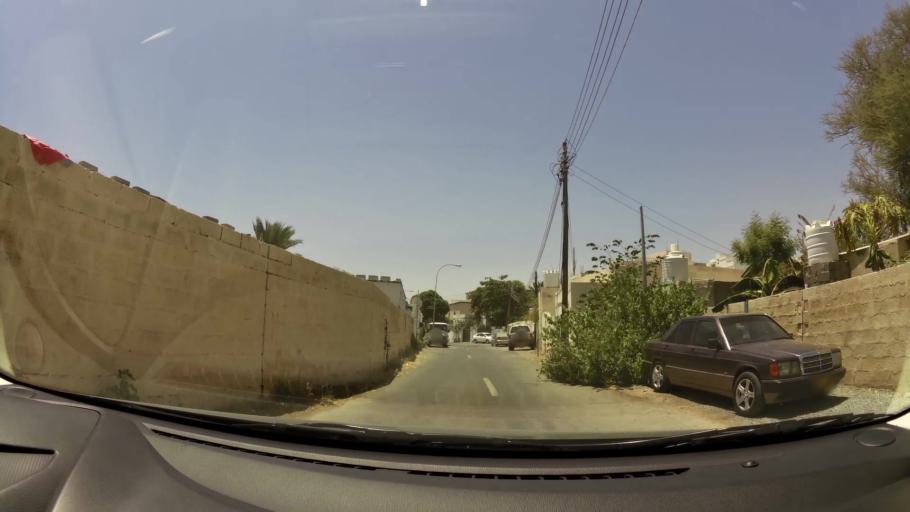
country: OM
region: Muhafazat Masqat
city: As Sib al Jadidah
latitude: 23.6247
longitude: 58.2423
